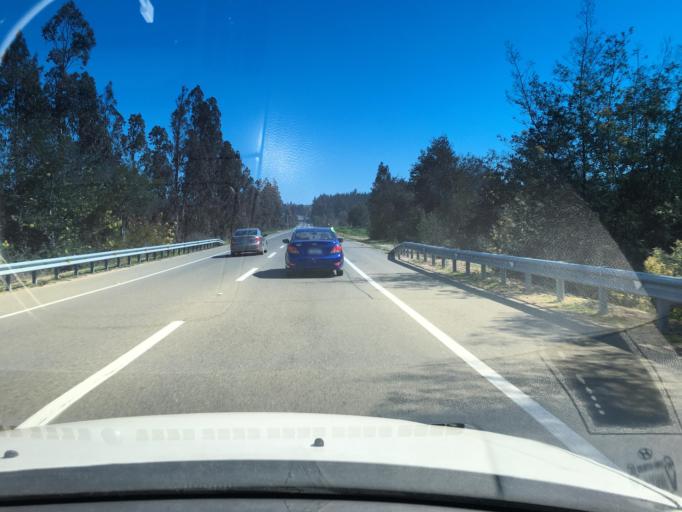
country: CL
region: Valparaiso
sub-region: San Antonio Province
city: El Tabo
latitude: -33.3895
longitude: -71.4711
